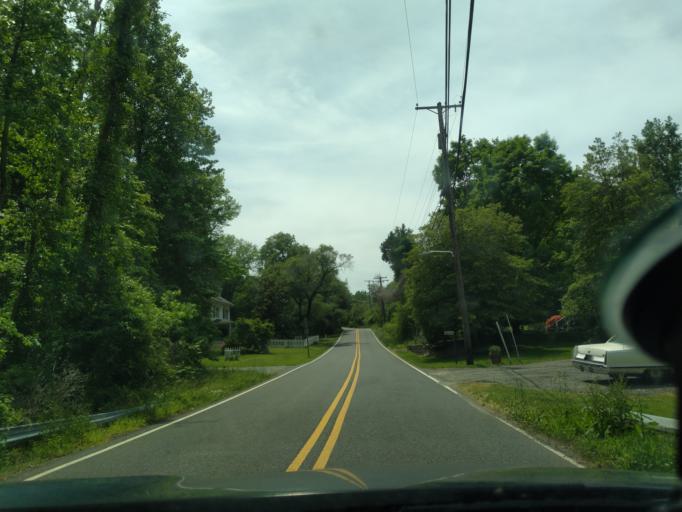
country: US
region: Maryland
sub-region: Calvert County
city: Owings
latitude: 38.7169
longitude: -76.6038
